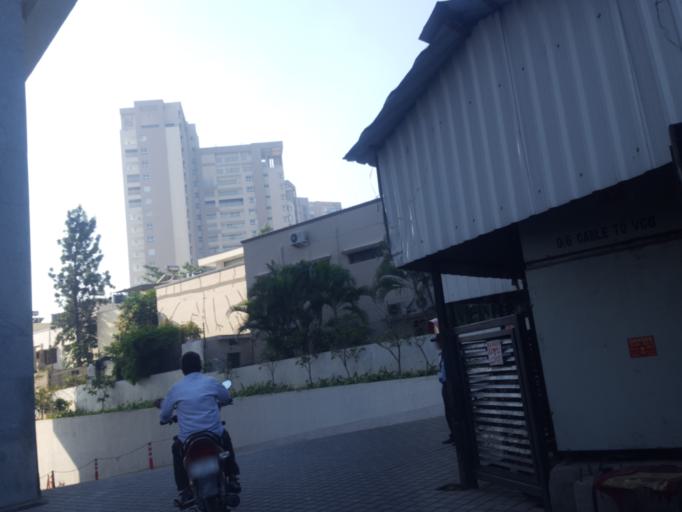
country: IN
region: Telangana
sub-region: Rangareddi
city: Kukatpalli
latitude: 17.4524
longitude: 78.3624
